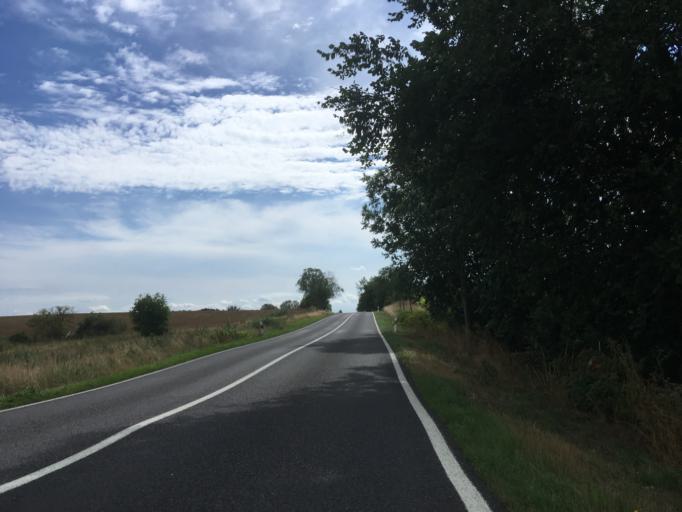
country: DE
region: Brandenburg
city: Gerswalde
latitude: 53.1778
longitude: 13.7422
